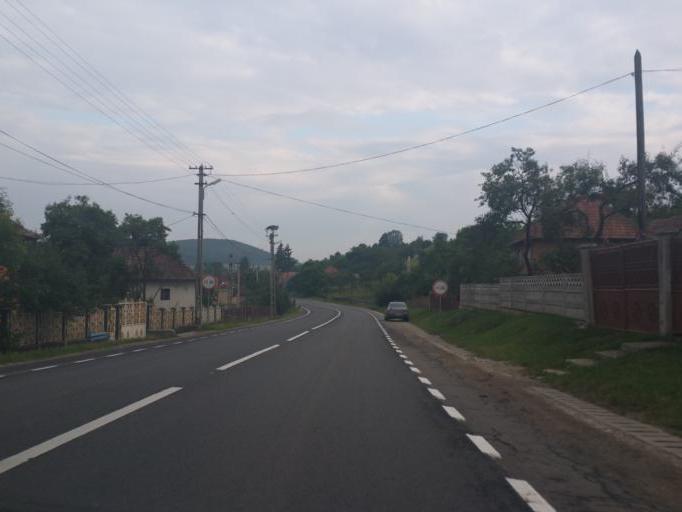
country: RO
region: Cluj
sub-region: Comuna Sanpaul
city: Sanpaul
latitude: 46.9090
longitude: 23.4169
